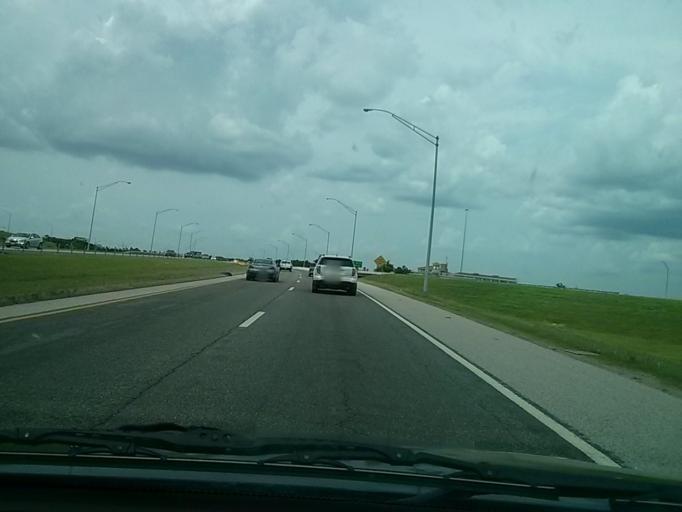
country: US
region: Oklahoma
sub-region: Tulsa County
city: Broken Arrow
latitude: 36.0295
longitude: -95.8620
